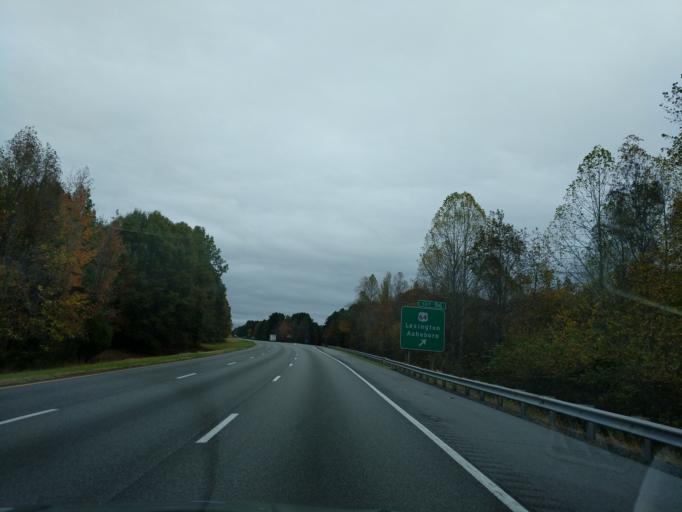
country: US
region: North Carolina
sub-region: Davidson County
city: Lexington
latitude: 35.8056
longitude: -80.1862
